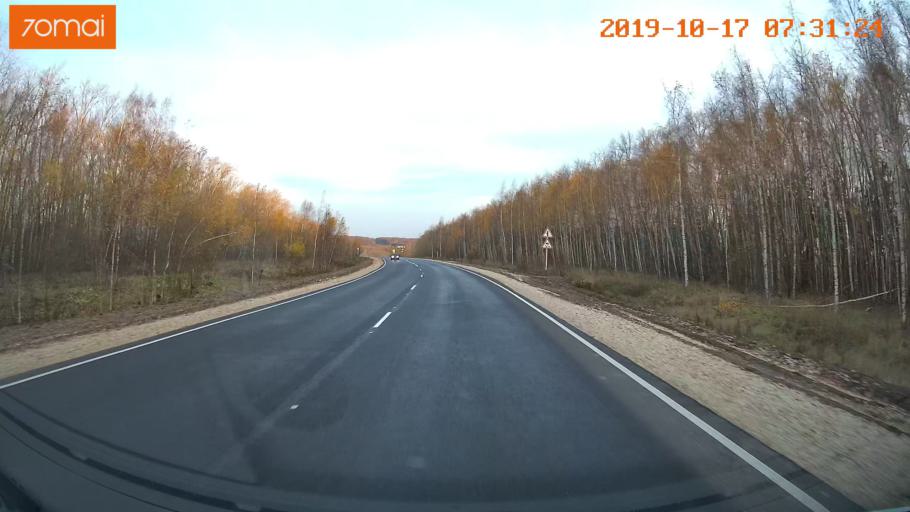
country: RU
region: Ivanovo
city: Gavrilov Posad
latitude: 56.3889
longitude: 39.9970
